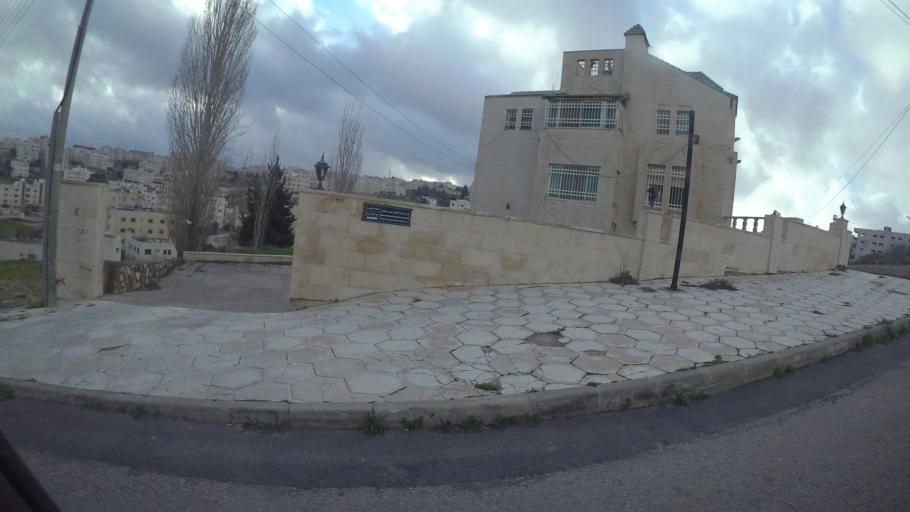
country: JO
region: Amman
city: Al Jubayhah
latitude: 32.0539
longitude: 35.8928
